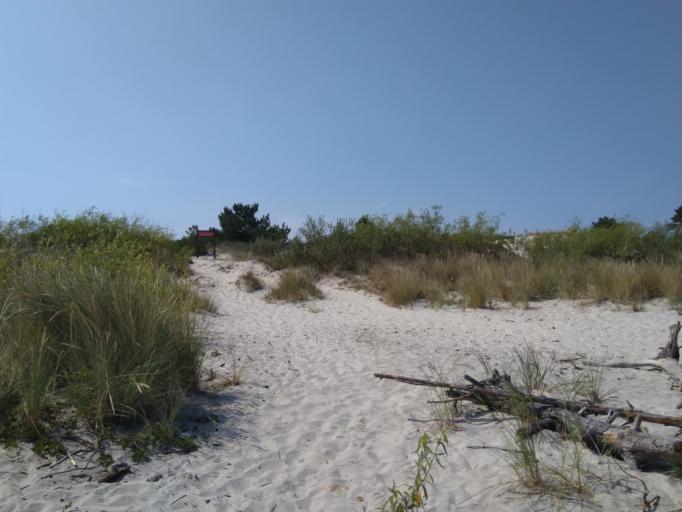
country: PL
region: Pomeranian Voivodeship
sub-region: Powiat pucki
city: Hel
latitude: 54.6581
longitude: 18.7729
